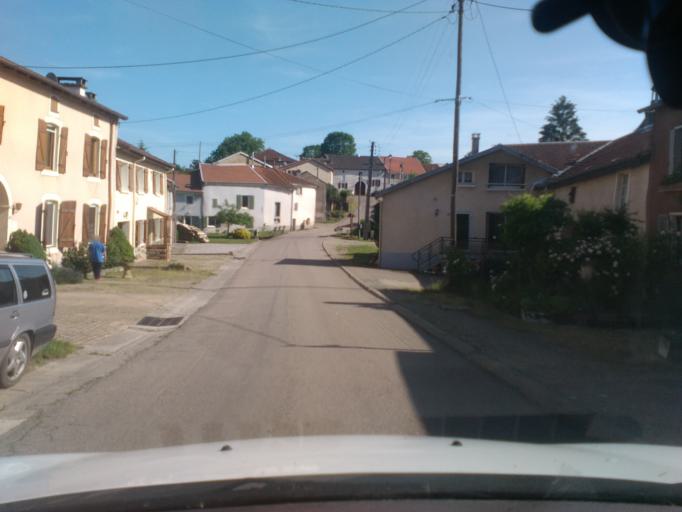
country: FR
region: Lorraine
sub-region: Departement des Vosges
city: Mirecourt
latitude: 48.3414
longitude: 6.1948
